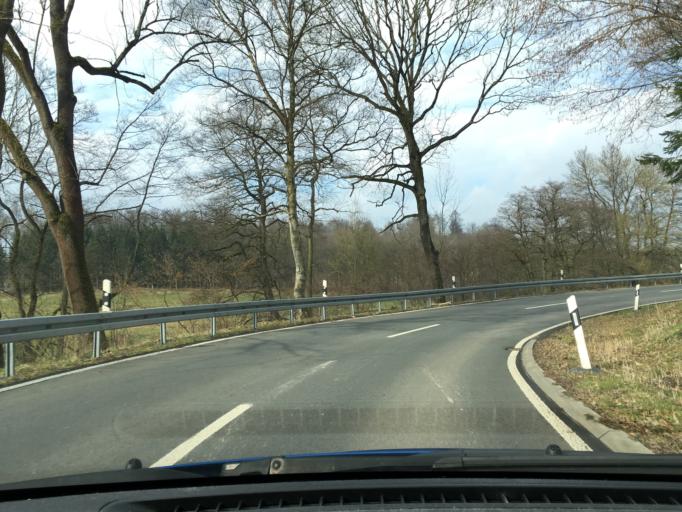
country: DE
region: Lower Saxony
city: Adelebsen
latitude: 51.5662
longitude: 9.7156
